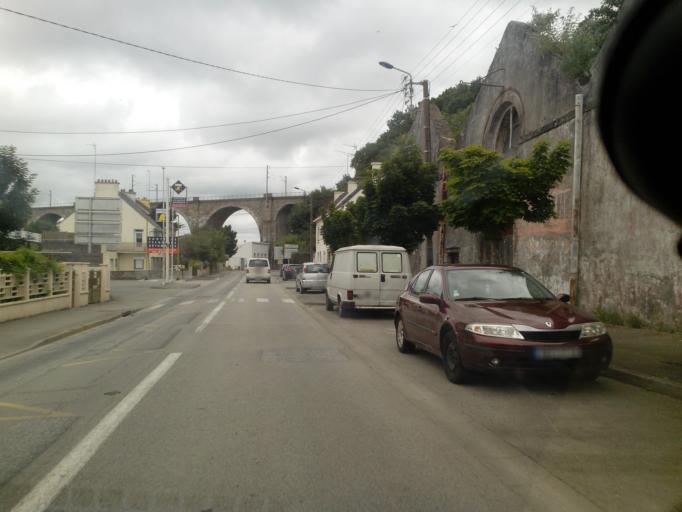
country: FR
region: Brittany
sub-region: Departement du Morbihan
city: Hennebont
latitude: 47.7969
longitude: -3.2752
